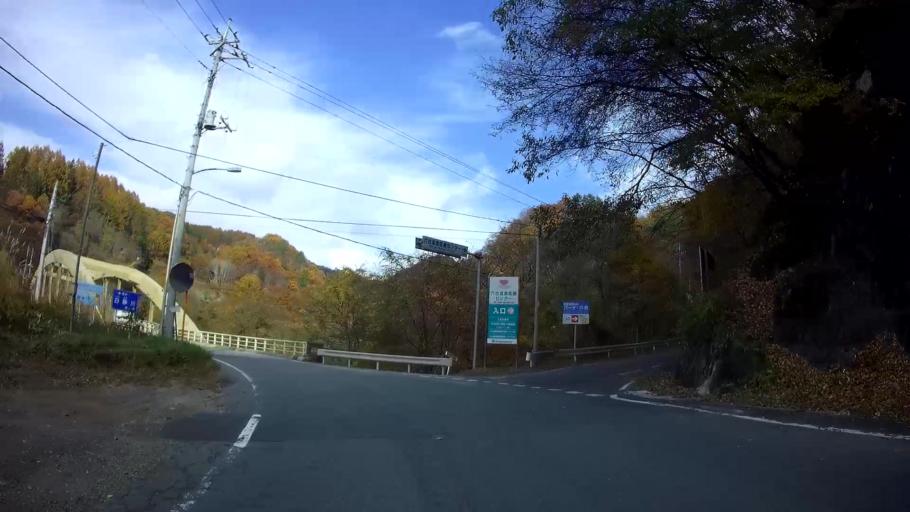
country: JP
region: Gunma
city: Nakanojomachi
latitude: 36.6506
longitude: 138.6512
